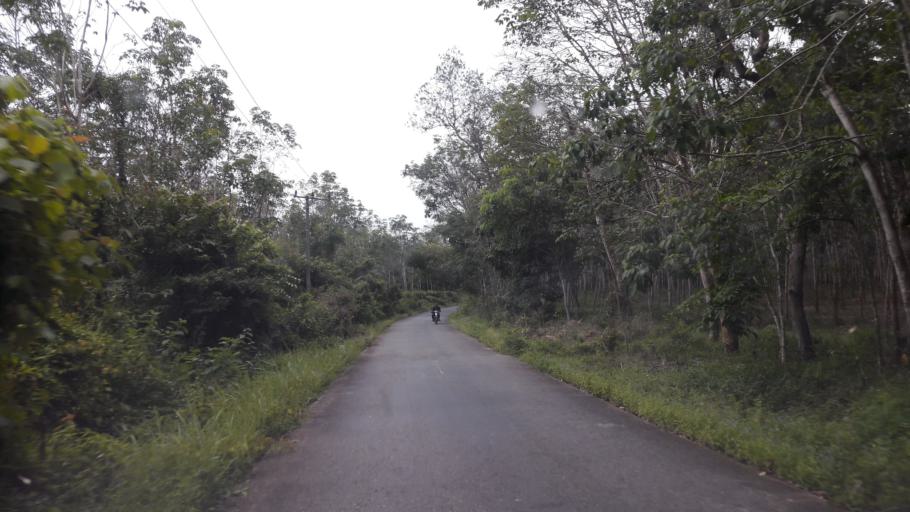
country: ID
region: South Sumatra
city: Gunungmenang
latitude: -3.1270
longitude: 104.1116
